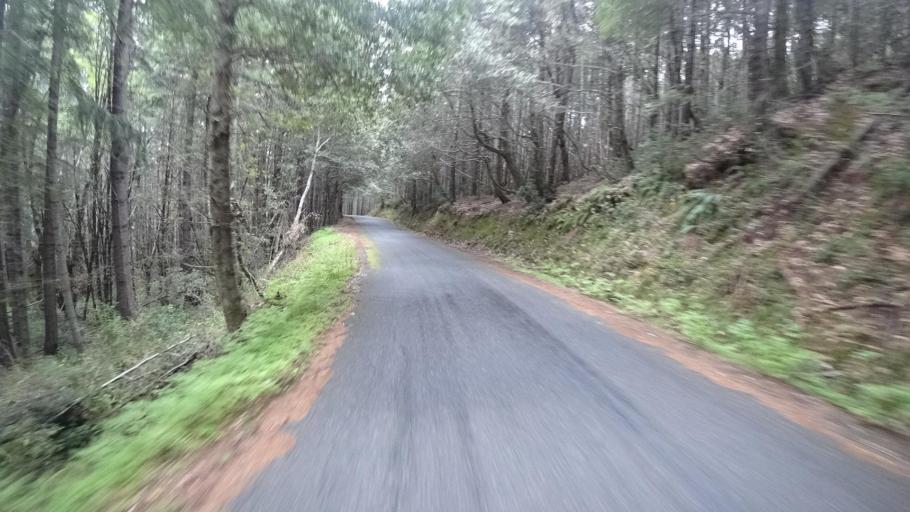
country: US
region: California
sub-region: Humboldt County
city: Willow Creek
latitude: 41.2034
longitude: -123.7746
